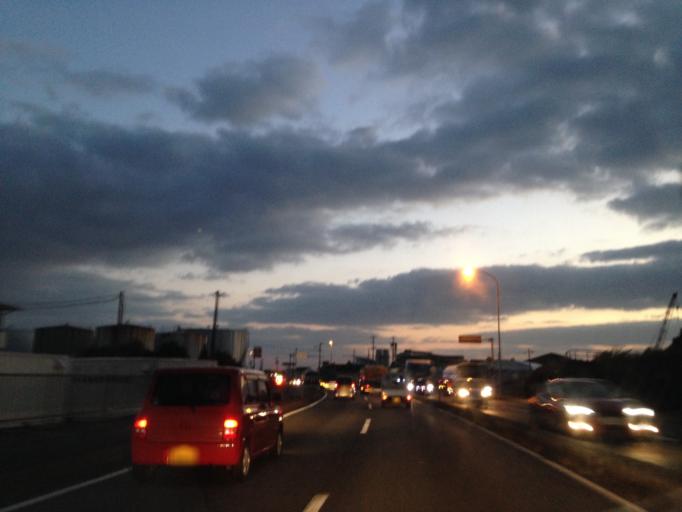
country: JP
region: Mie
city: Yokkaichi
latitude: 35.0084
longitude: 136.6719
